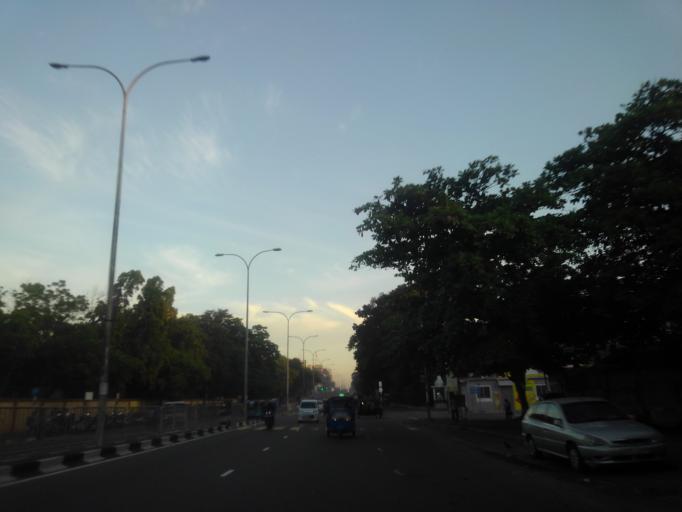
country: LK
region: Western
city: Kolonnawa
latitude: 6.9176
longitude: 79.8777
